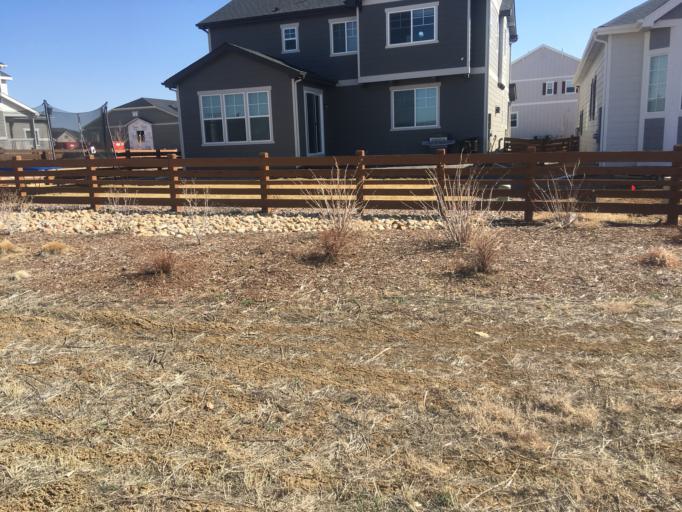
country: US
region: Colorado
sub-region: Boulder County
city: Erie
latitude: 40.0578
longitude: -105.0276
